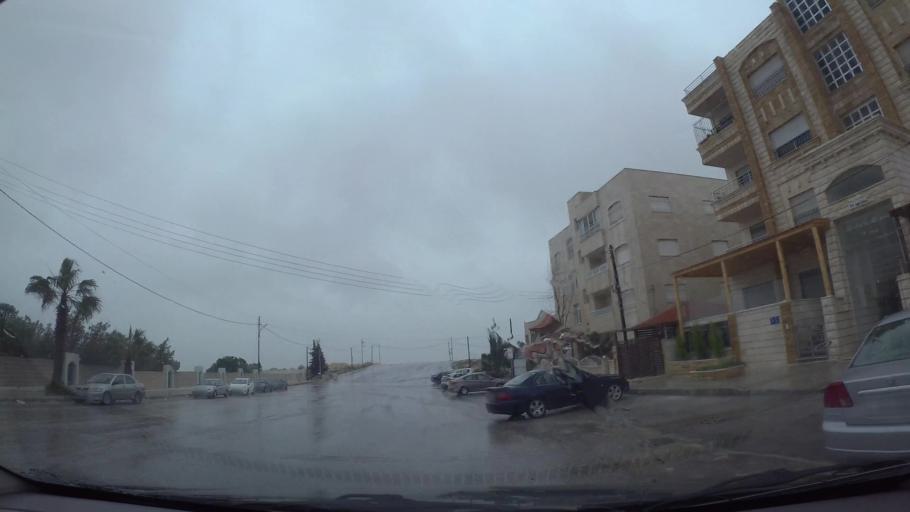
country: JO
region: Amman
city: Al Jubayhah
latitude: 32.0147
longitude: 35.8938
